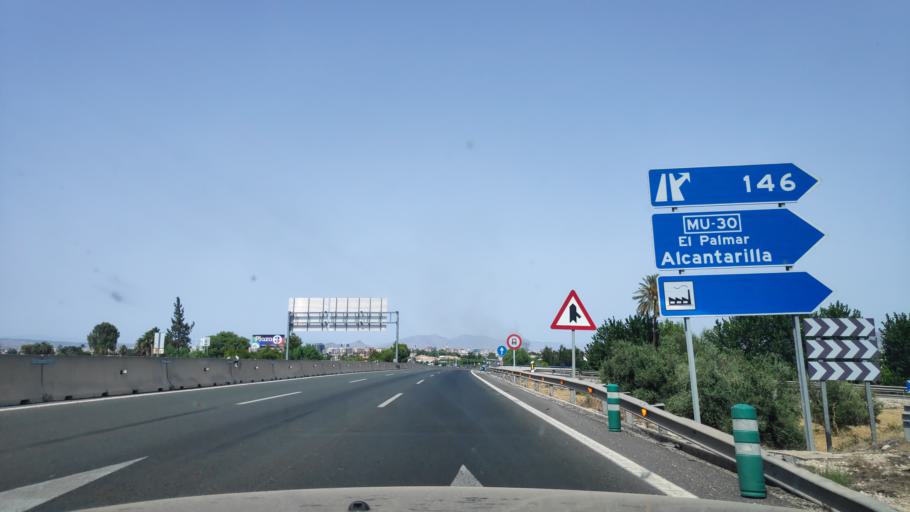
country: ES
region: Murcia
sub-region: Murcia
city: Murcia
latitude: 37.9485
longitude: -1.1455
